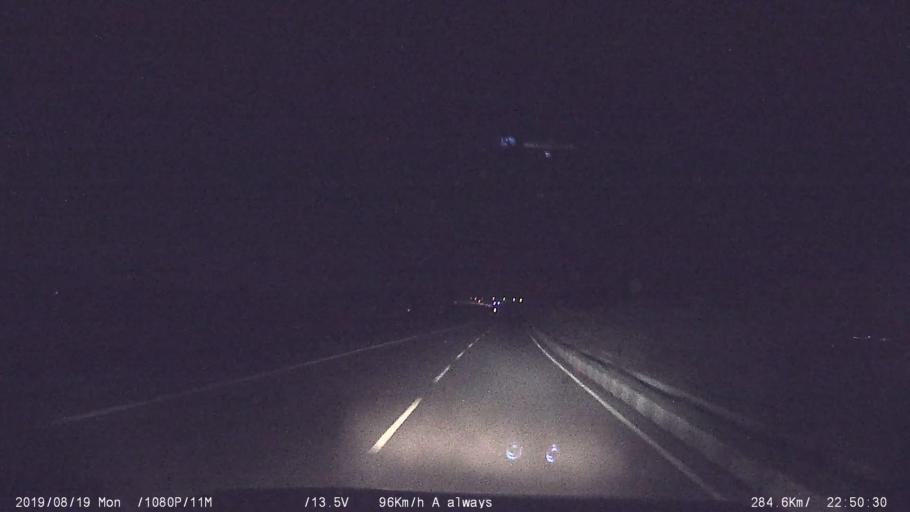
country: IN
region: Tamil Nadu
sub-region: Erode
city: Vijayapuri
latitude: 11.2395
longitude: 77.4981
